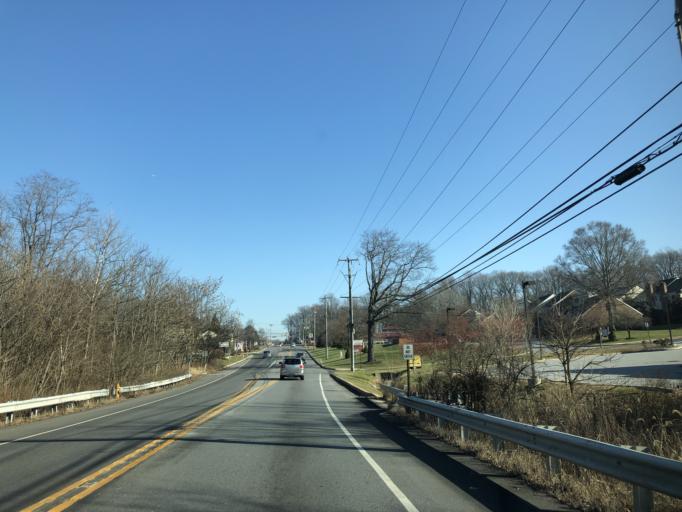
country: US
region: Pennsylvania
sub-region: Chester County
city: Downingtown
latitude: 40.0308
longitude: -75.6816
